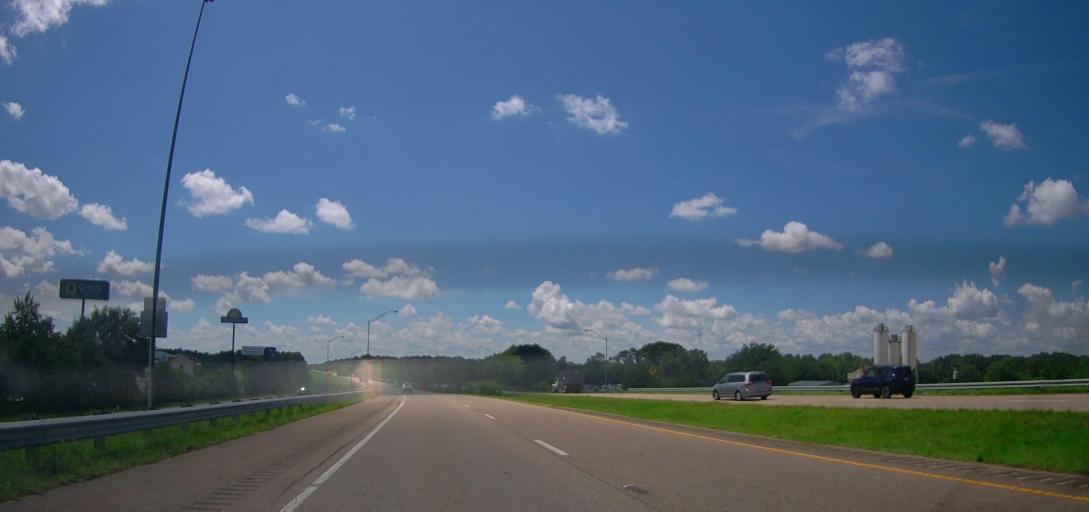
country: US
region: Alabama
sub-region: Elmore County
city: Blue Ridge
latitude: 32.4213
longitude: -86.2305
